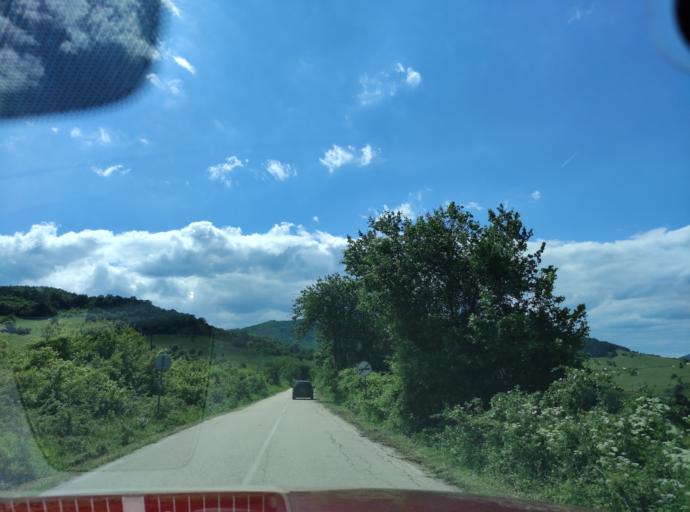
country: BG
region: Vidin
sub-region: Obshtina Ruzhintsi
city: Ruzhintsi
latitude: 43.5010
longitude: 22.7658
